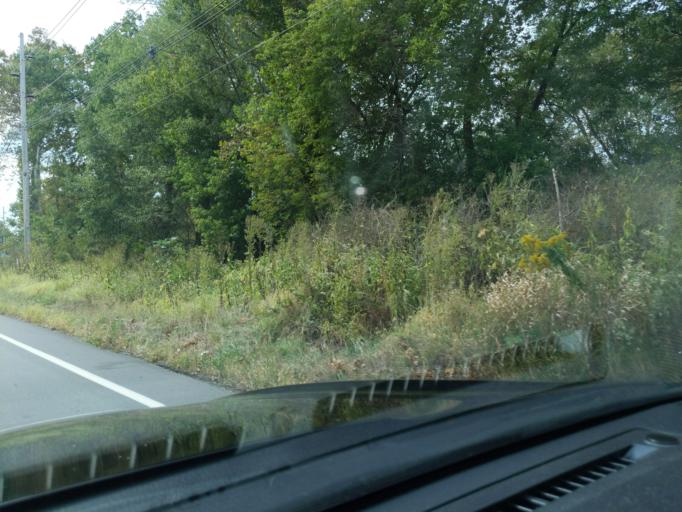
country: US
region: Pennsylvania
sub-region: Blair County
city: Hollidaysburg
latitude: 40.4416
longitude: -78.3543
